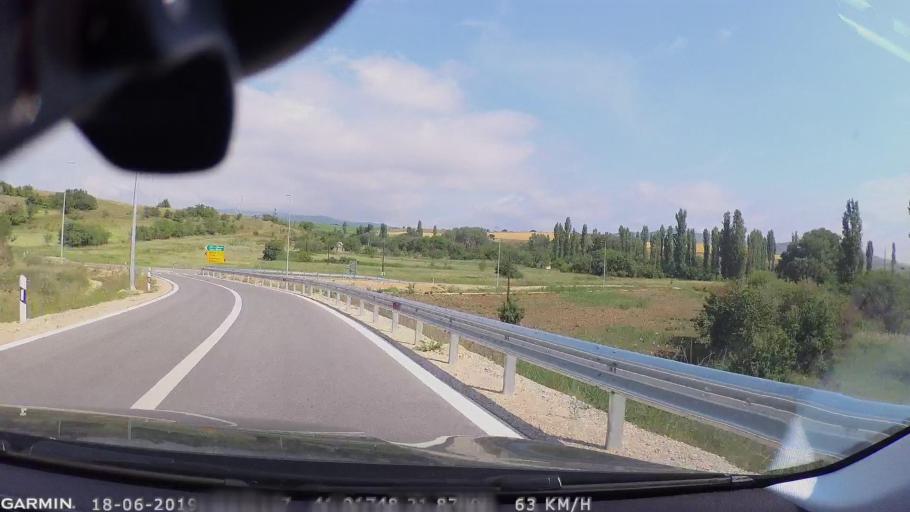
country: MK
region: Sveti Nikole
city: Gorobinci
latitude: 41.9148
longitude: 21.8846
